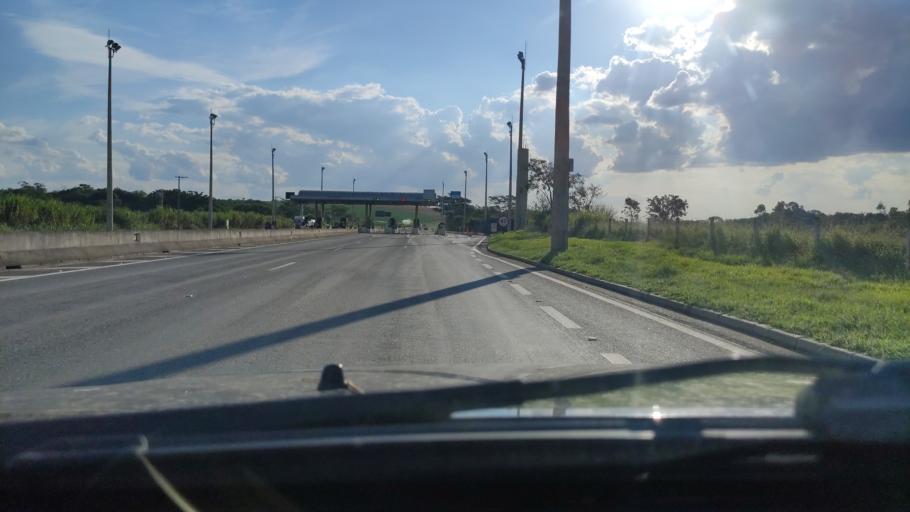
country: BR
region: Sao Paulo
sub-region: Mogi-Mirim
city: Mogi Mirim
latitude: -22.4565
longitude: -46.9008
